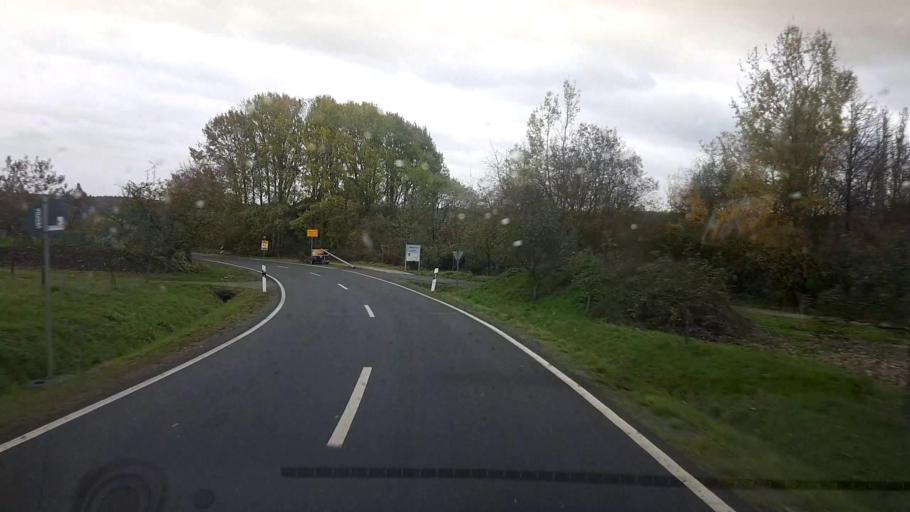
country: DE
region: Bavaria
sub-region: Upper Franconia
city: Burgwindheim
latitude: 49.8758
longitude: 10.5578
